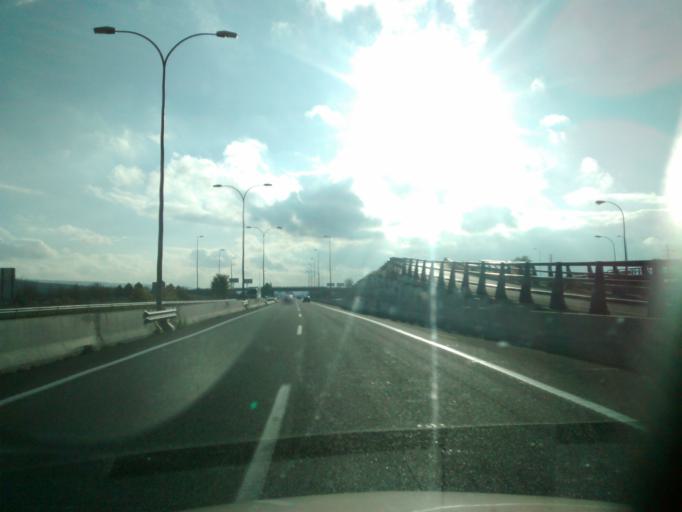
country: ES
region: Castille-La Mancha
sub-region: Provincia de Guadalajara
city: Cabanillas del Campo
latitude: 40.6223
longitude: -3.1999
